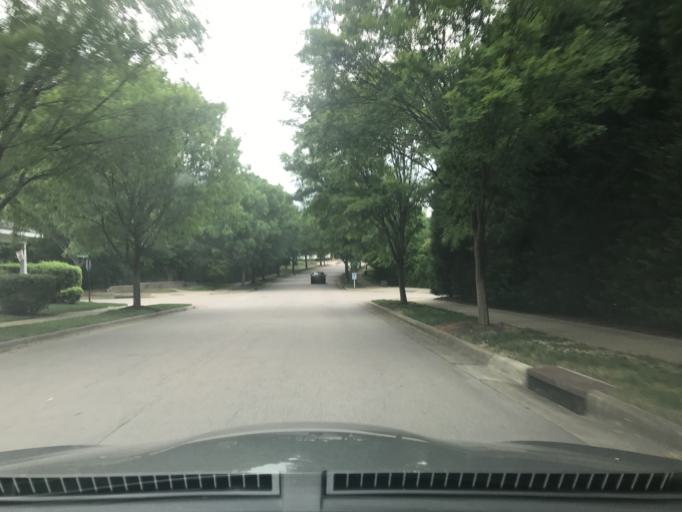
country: US
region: North Carolina
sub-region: Wake County
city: Wake Forest
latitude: 35.9210
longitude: -78.5641
